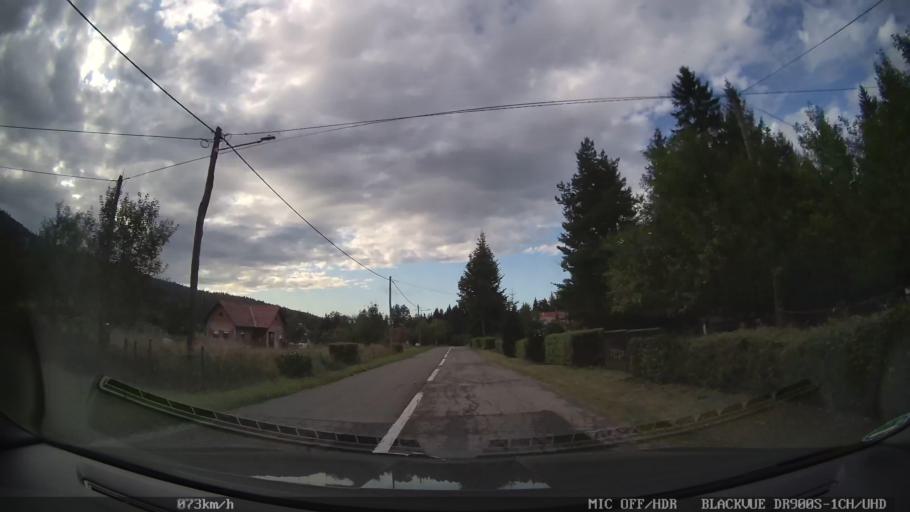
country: HR
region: Licko-Senjska
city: Jezerce
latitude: 44.9502
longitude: 15.5336
